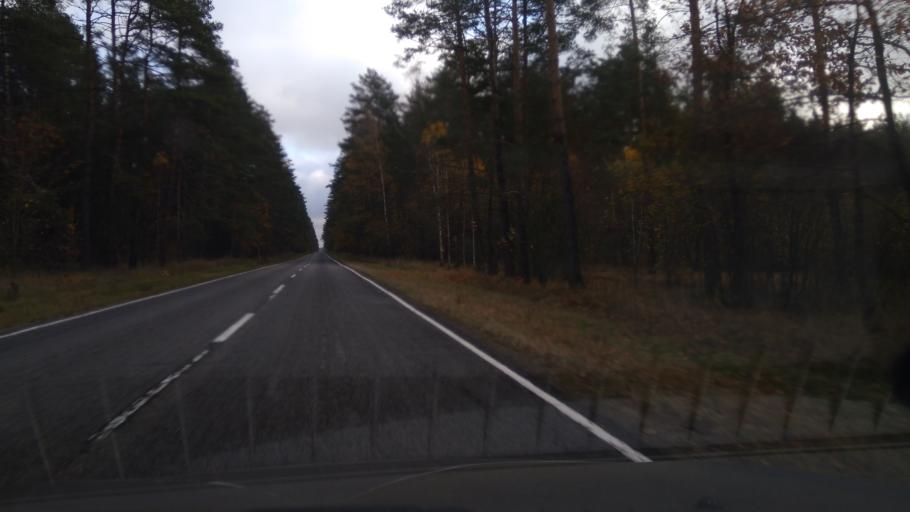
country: BY
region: Minsk
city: Slutsk
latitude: 53.2308
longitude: 27.6745
